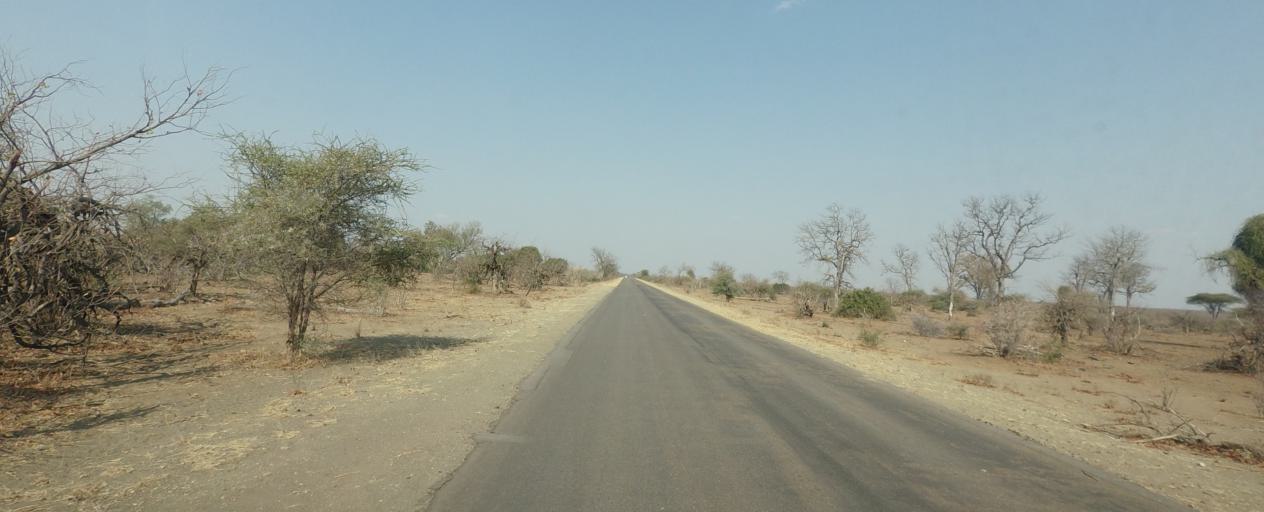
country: ZA
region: Limpopo
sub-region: Mopani District Municipality
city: Giyani
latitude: -23.0971
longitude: 31.3992
